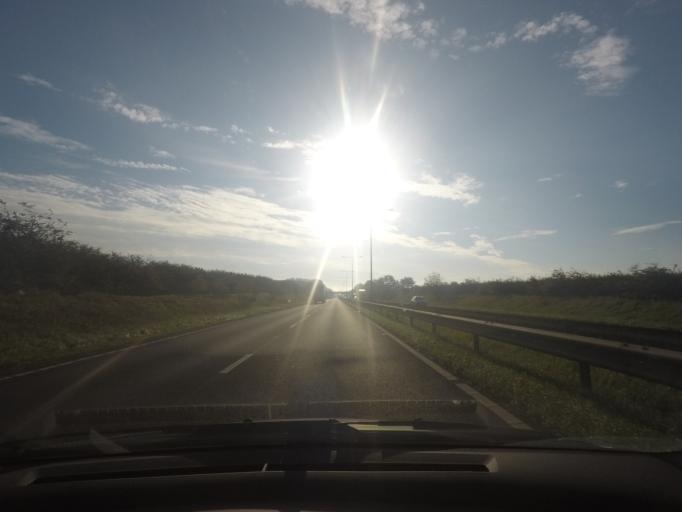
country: GB
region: England
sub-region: East Riding of Yorkshire
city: Brantingham
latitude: 53.7532
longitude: -0.5815
